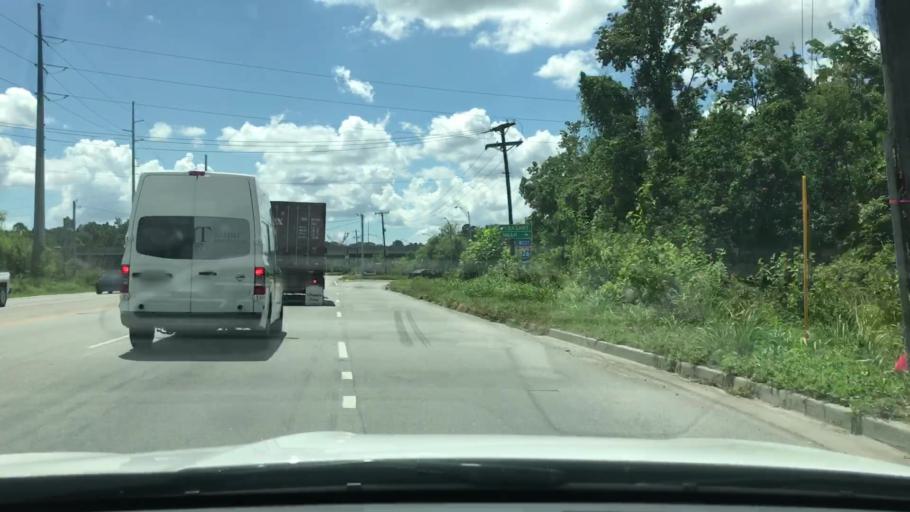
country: US
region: South Carolina
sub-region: Berkeley County
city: Hanahan
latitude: 32.8967
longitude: -79.9857
